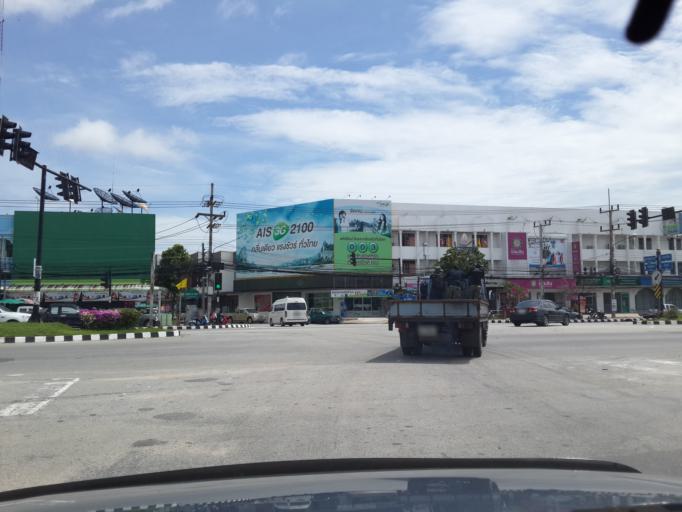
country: TH
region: Narathiwat
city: Narathiwat
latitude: 6.4162
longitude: 101.8114
